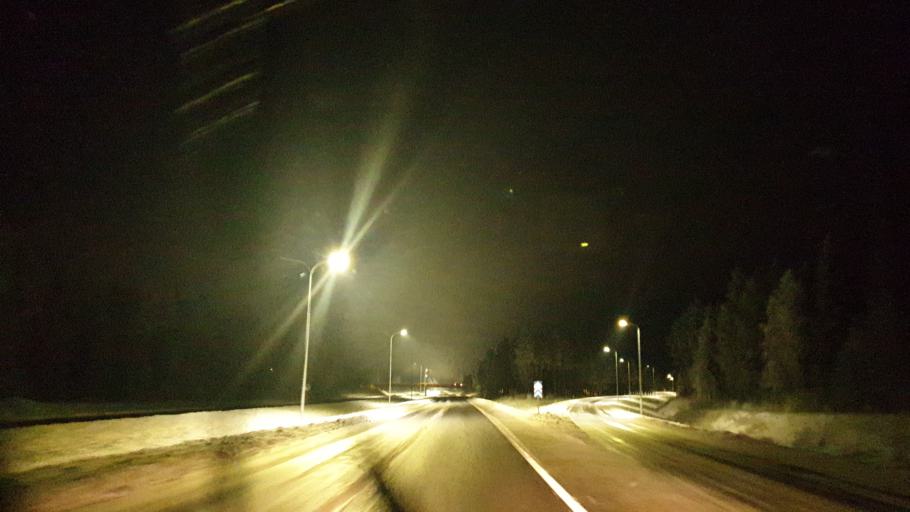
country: FI
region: Northern Ostrobothnia
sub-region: Oulu
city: Haukipudas
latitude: 65.1663
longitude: 25.4260
